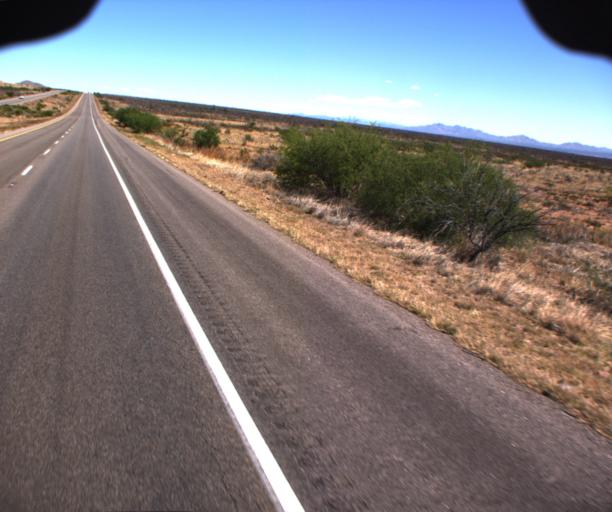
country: US
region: Arizona
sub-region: Cochise County
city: Huachuca City
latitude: 31.7885
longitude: -110.3499
